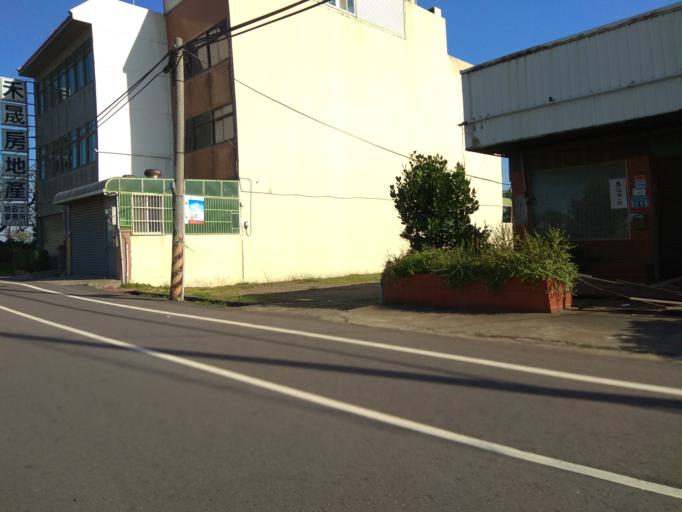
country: TW
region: Taiwan
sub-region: Hsinchu
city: Zhubei
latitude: 25.0294
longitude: 121.0683
